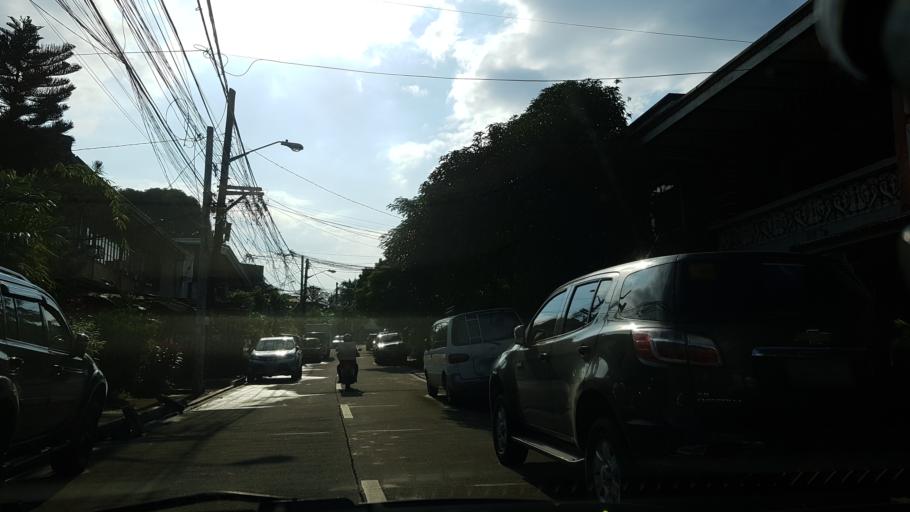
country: PH
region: Metro Manila
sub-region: Quezon City
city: Quezon City
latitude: 14.6416
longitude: 121.0510
